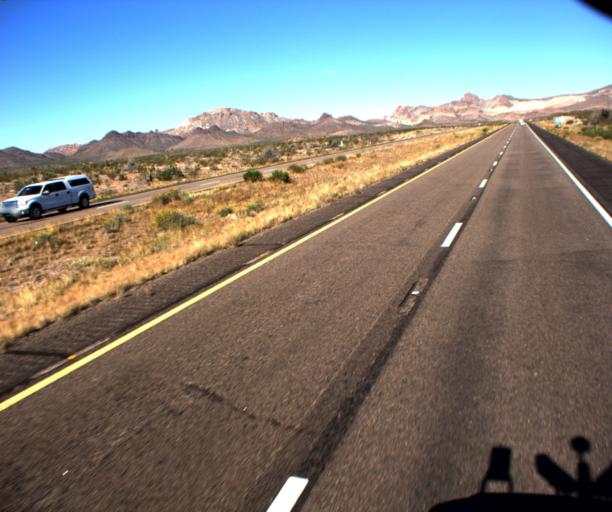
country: US
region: Arizona
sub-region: Mohave County
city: Golden Valley
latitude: 35.2280
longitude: -114.3385
